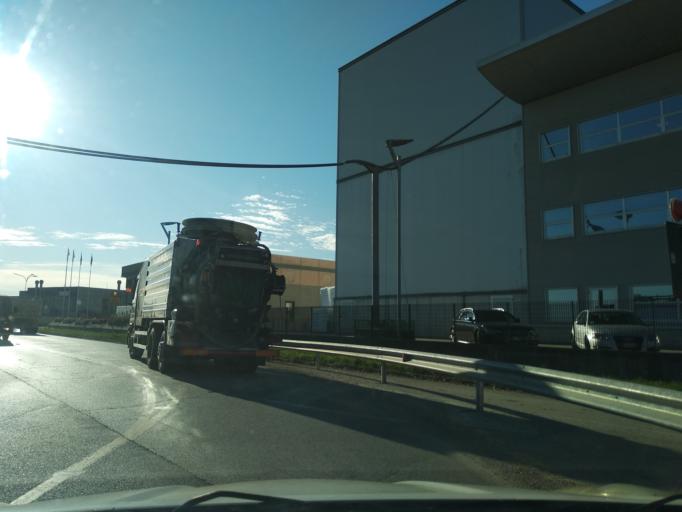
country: IT
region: Veneto
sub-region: Provincia di Vicenza
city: Quinto Vicentino
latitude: 45.5885
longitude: 11.6439
